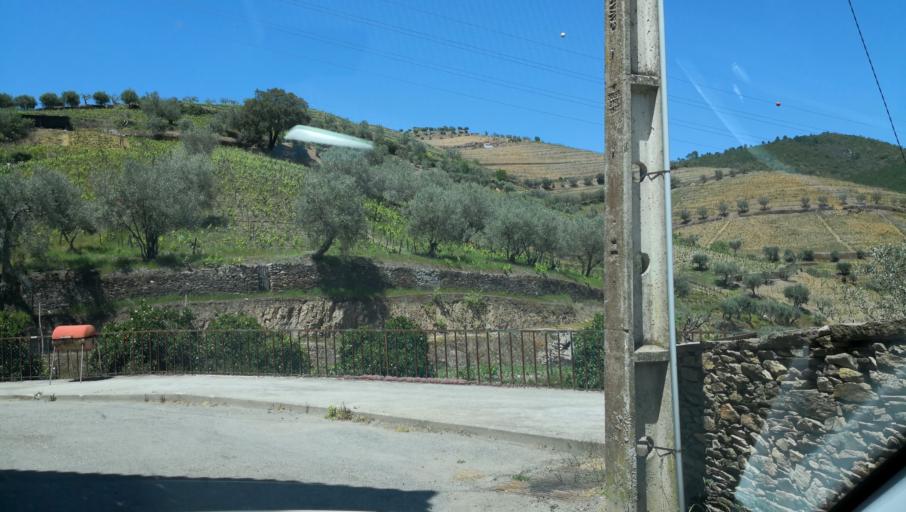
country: PT
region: Vila Real
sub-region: Vila Real
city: Vila Real
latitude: 41.2278
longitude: -7.7204
